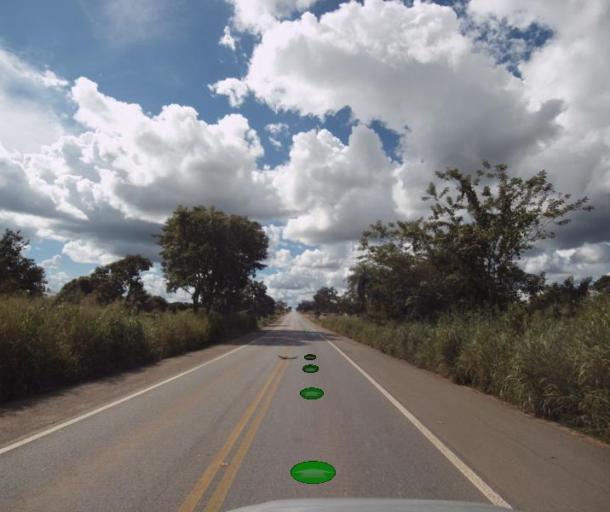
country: BR
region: Goias
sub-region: Porangatu
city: Porangatu
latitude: -13.4278
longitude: -49.1301
